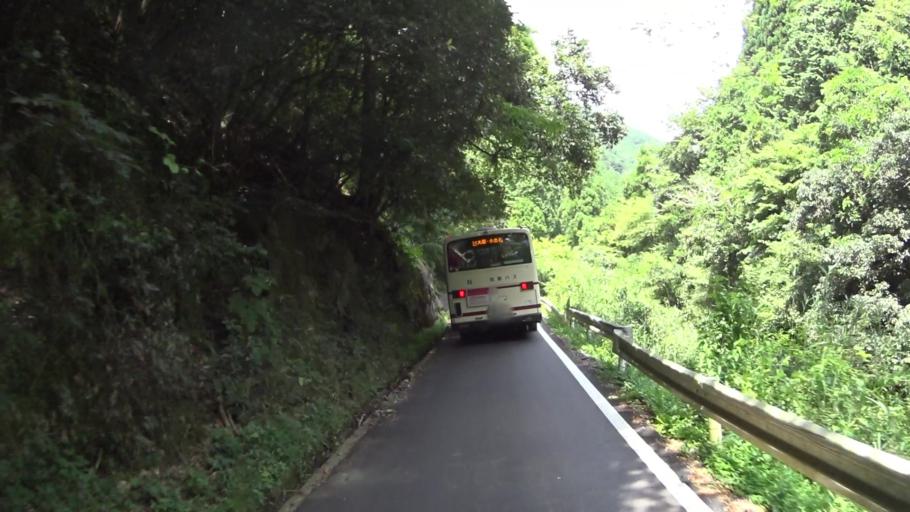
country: JP
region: Shiga Prefecture
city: Kitahama
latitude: 35.1279
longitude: 135.8319
